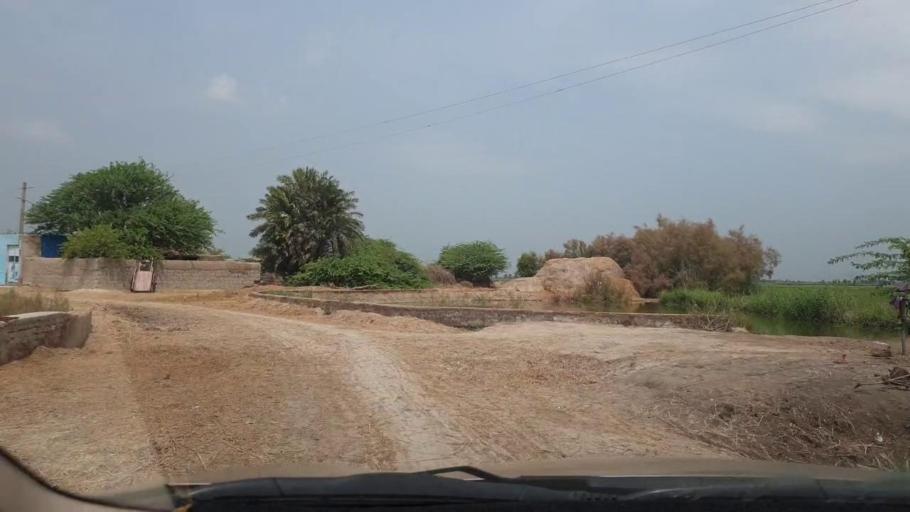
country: PK
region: Sindh
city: Larkana
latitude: 27.5236
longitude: 68.1209
